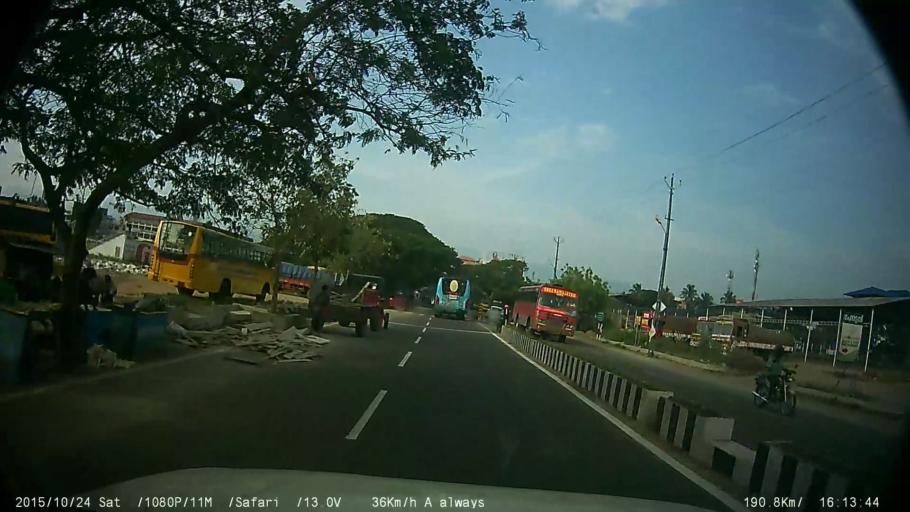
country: IN
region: Kerala
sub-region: Palakkad district
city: Palakkad
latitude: 10.7713
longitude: 76.6623
